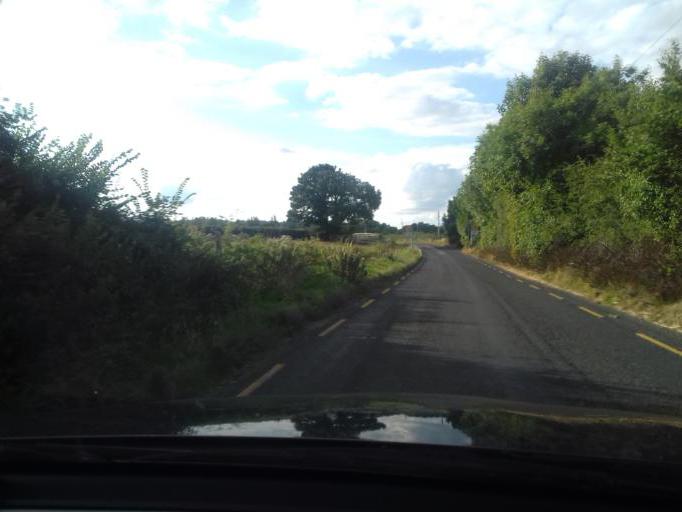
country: IE
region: Leinster
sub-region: Kilkenny
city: Graiguenamanagh
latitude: 52.5870
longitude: -6.9598
